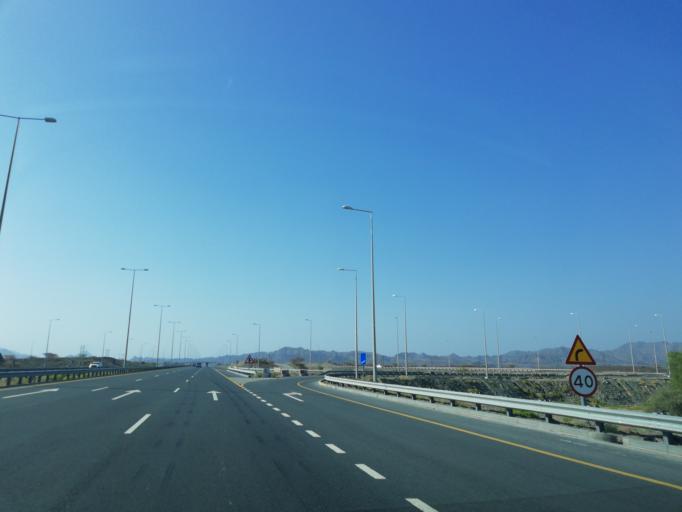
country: OM
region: Muhafazat ad Dakhiliyah
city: Sufalat Sama'il
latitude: 23.0507
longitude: 58.1939
